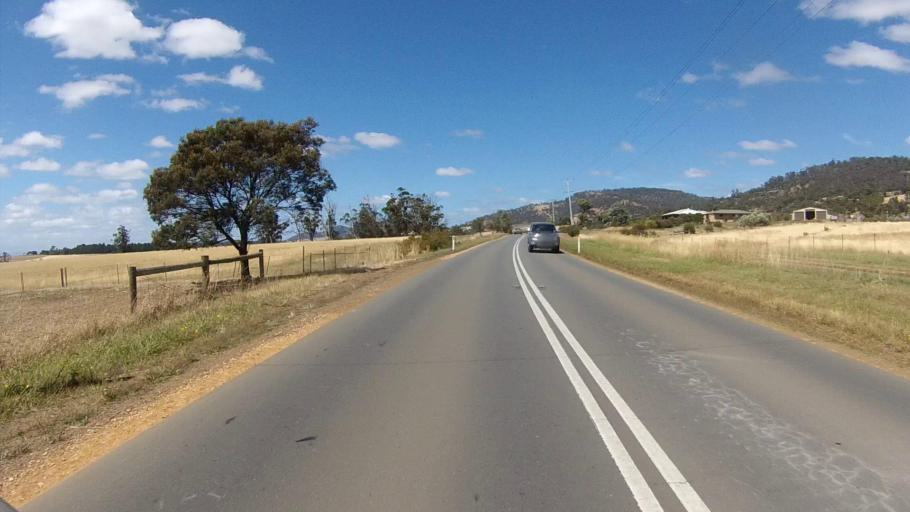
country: AU
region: Tasmania
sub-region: Clarence
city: Cambridge
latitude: -42.7769
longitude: 147.4168
